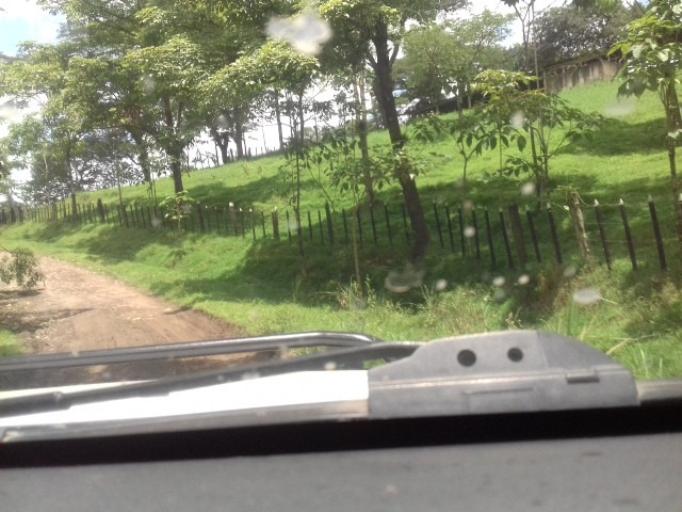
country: NI
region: Matagalpa
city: Rio Blanco
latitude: 12.9848
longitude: -85.3770
